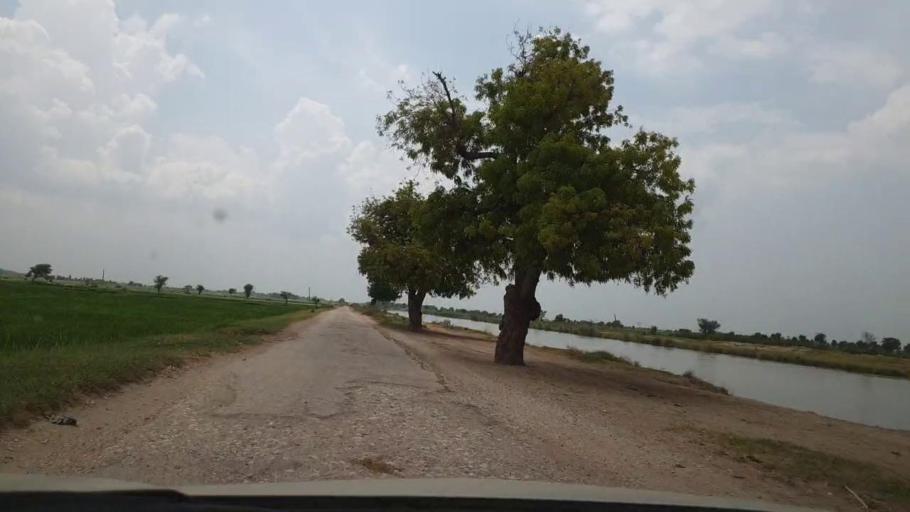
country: PK
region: Sindh
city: Goth Garelo
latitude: 27.4302
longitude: 68.1077
